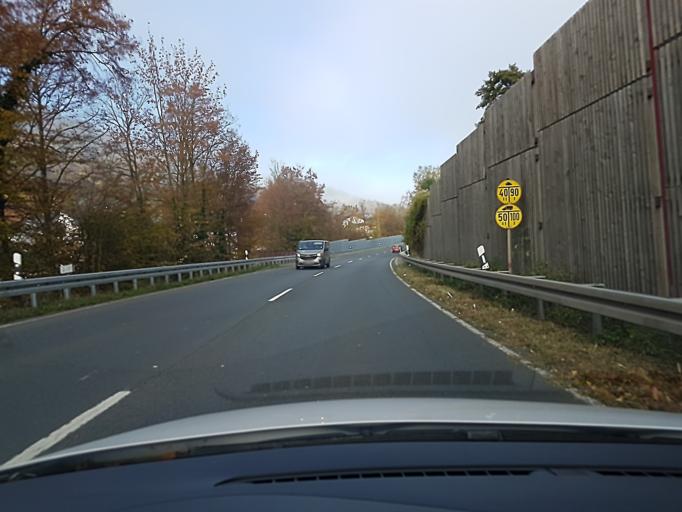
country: DE
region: Bavaria
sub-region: Regierungsbezirk Unterfranken
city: Kleinheubach
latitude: 49.7164
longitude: 9.2055
